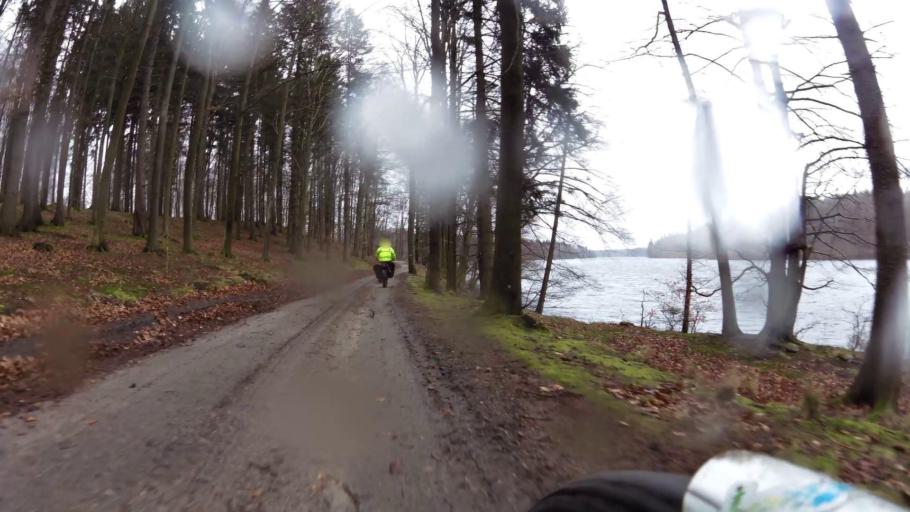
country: PL
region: Pomeranian Voivodeship
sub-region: Powiat bytowski
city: Miastko
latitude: 54.0604
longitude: 17.0753
